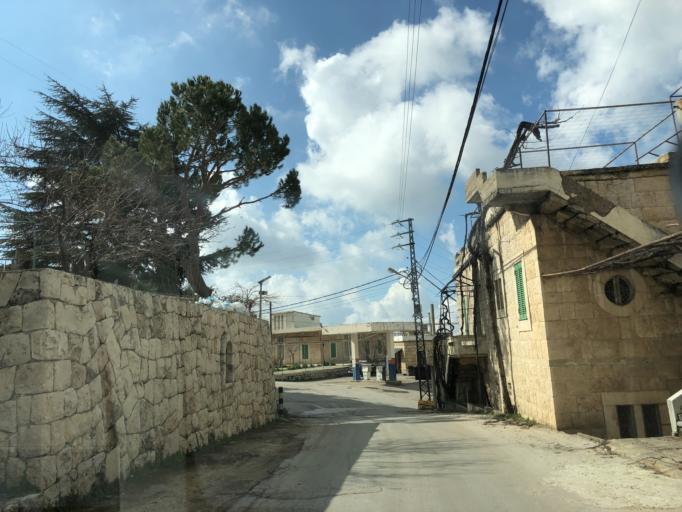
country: LB
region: Liban-Nord
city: Amioun
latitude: 34.2025
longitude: 35.8256
